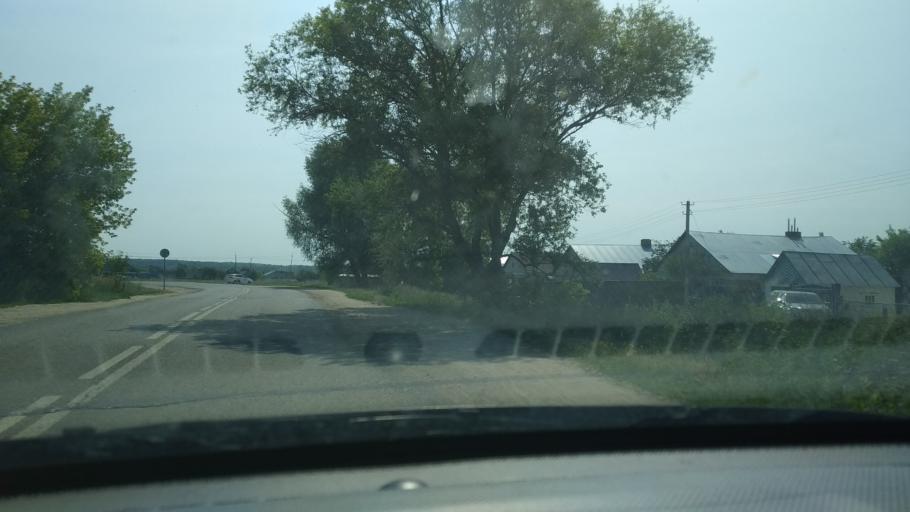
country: RU
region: Tatarstan
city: Osinovo
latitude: 55.9803
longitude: 48.8094
